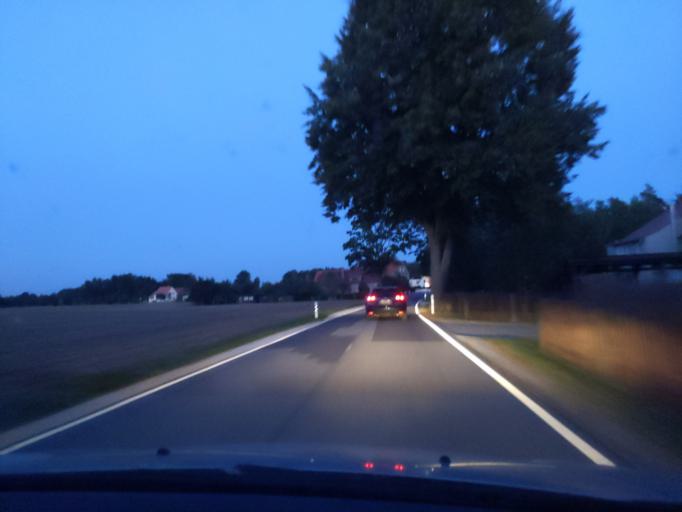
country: DE
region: Saxony
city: Grossdubrau
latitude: 51.2810
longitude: 14.5015
